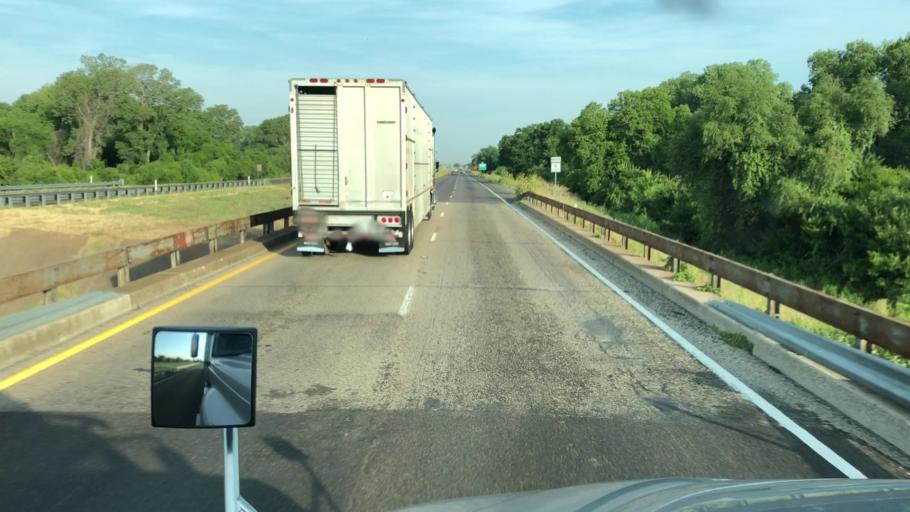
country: US
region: Texas
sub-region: McLennan County
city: Bellmead
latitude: 31.5402
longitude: -97.0456
